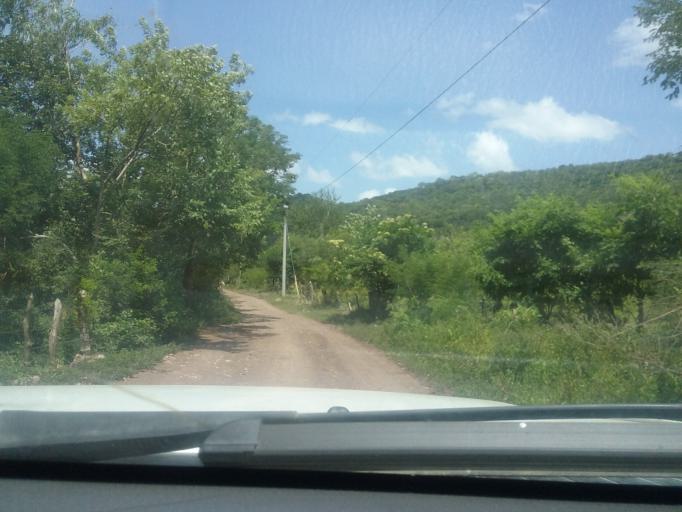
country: NI
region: Matagalpa
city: Terrabona
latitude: 12.6553
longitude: -86.0076
